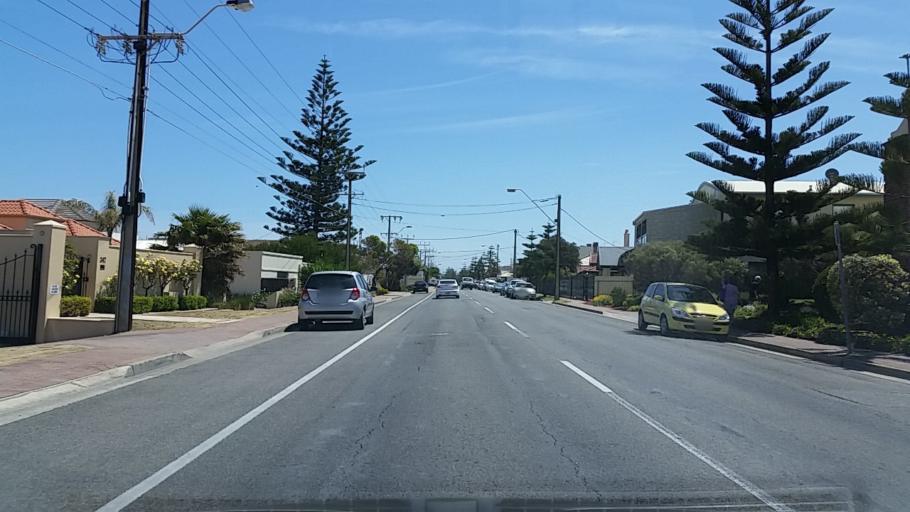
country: AU
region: South Australia
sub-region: Charles Sturt
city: Henley Beach
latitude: -34.9137
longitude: 138.4927
